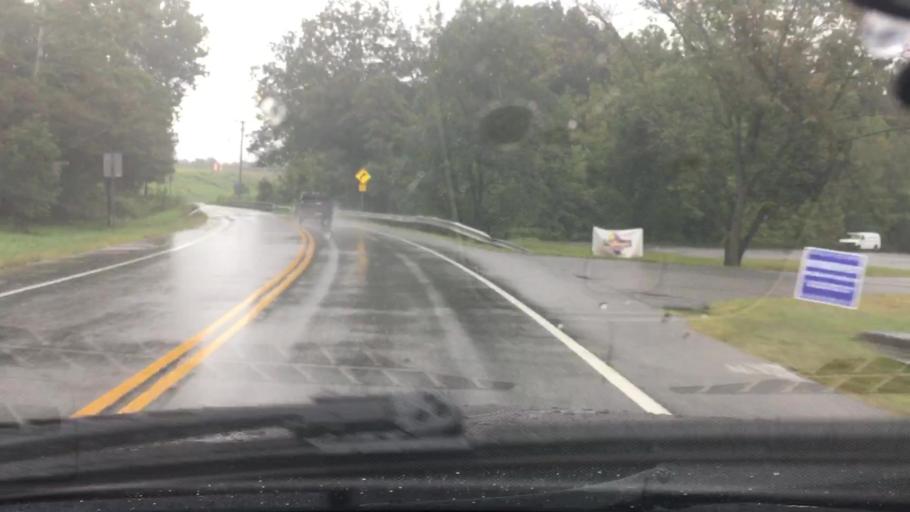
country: US
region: New York
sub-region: Dutchess County
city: Myers Corner
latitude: 41.6251
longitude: -73.8943
